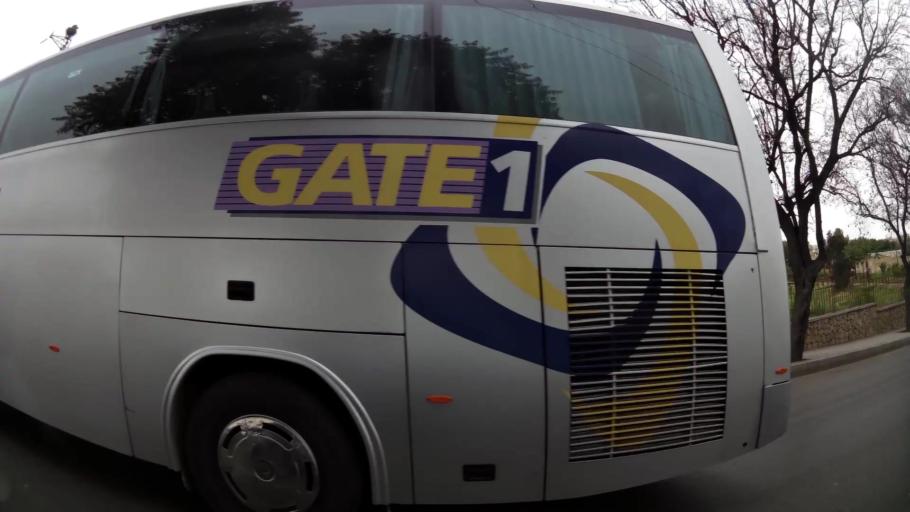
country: MA
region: Fes-Boulemane
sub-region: Fes
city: Fes
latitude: 34.0494
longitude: -4.9928
